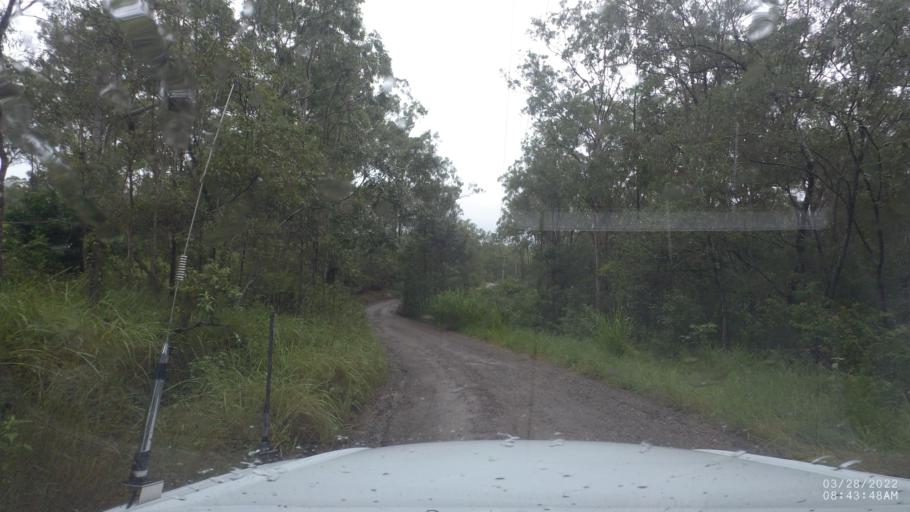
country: AU
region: Queensland
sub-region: Logan
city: Cedar Vale
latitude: -27.8378
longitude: 153.0643
